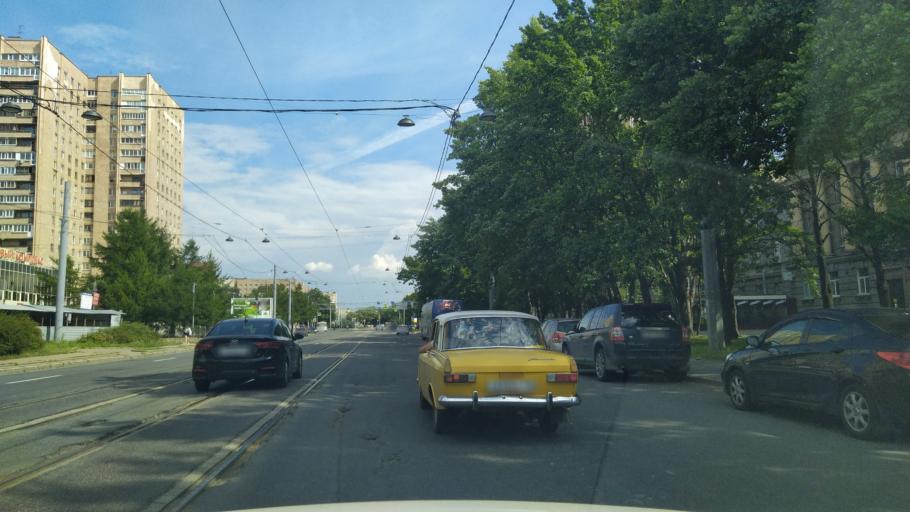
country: RU
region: St.-Petersburg
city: Kushelevka
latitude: 59.9991
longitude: 30.3580
